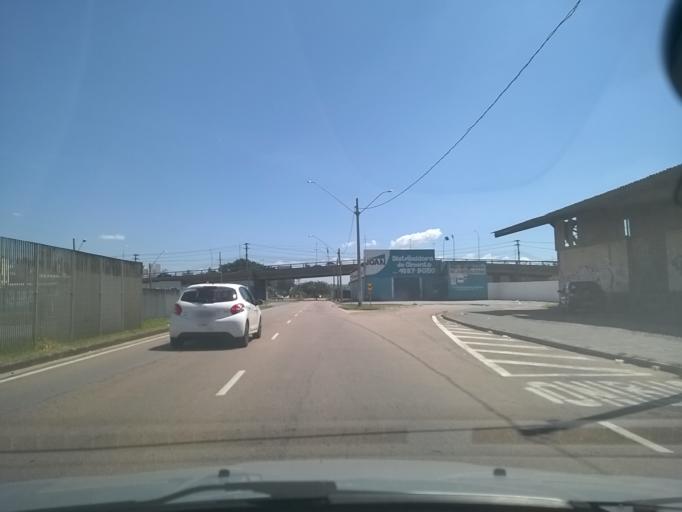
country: BR
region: Sao Paulo
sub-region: Jundiai
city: Jundiai
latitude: -23.1925
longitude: -46.8744
